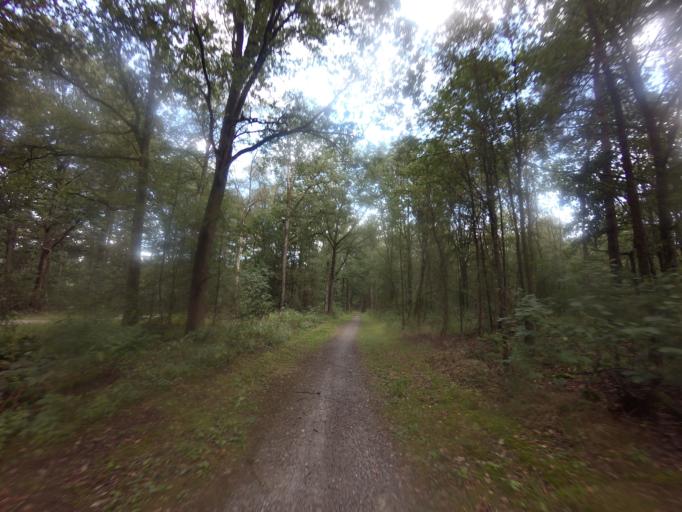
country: NL
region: Overijssel
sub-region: Gemeente Staphorst
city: Staphorst
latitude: 52.6483
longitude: 6.2656
